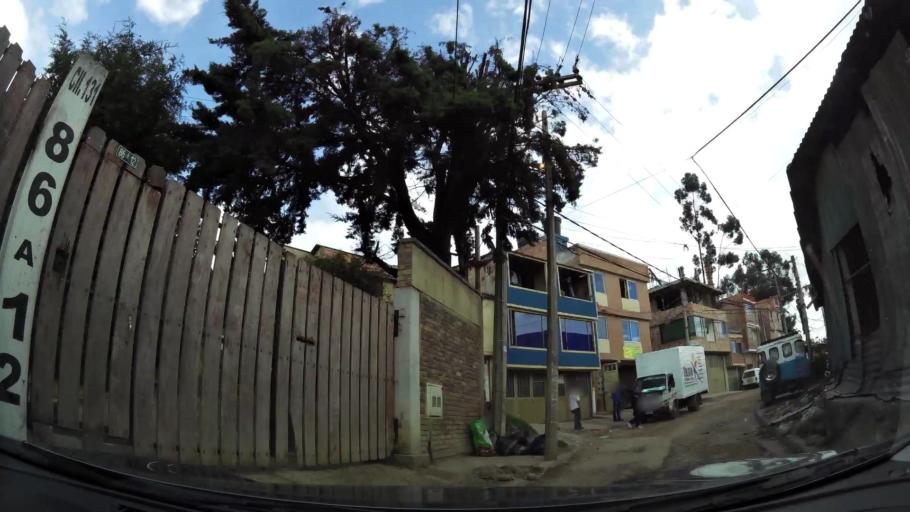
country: CO
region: Cundinamarca
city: Cota
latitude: 4.7271
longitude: -74.0844
